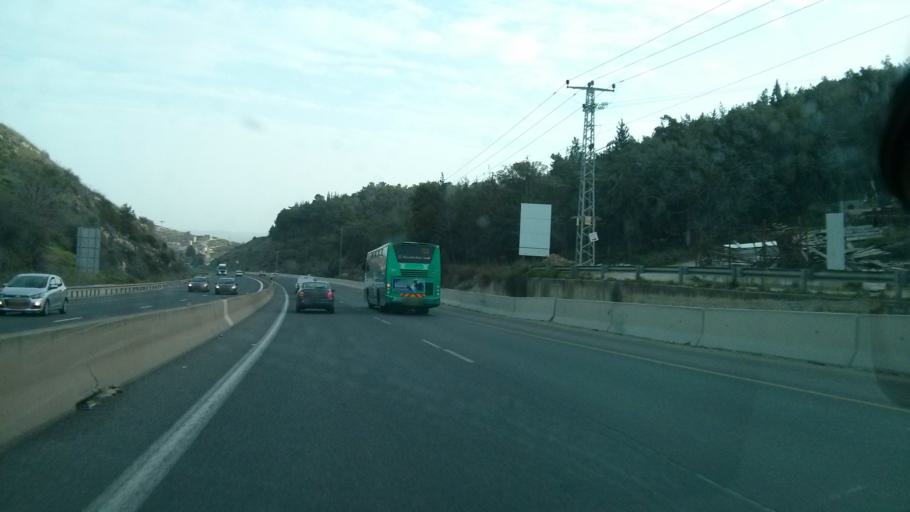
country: IL
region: Haifa
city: Umm el Fahm
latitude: 32.5441
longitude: 35.1596
